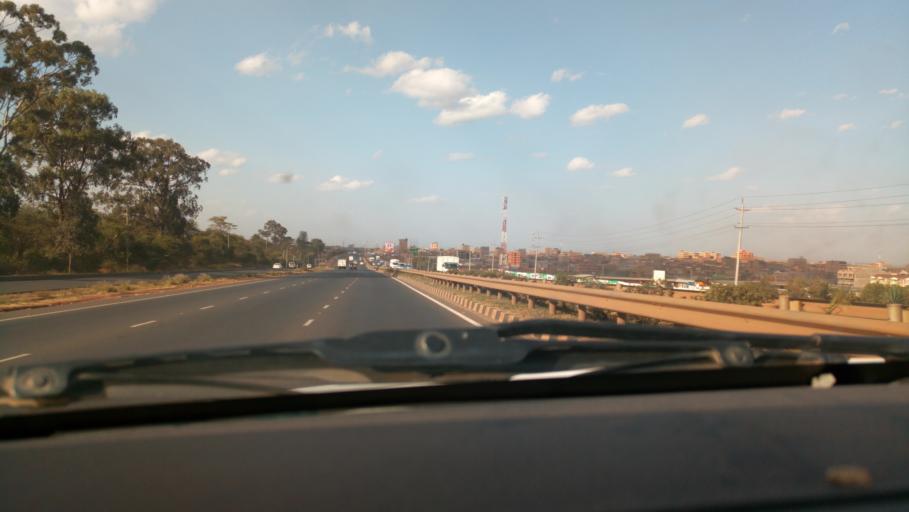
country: KE
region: Nairobi Area
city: Thika
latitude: -1.0731
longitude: 37.0477
